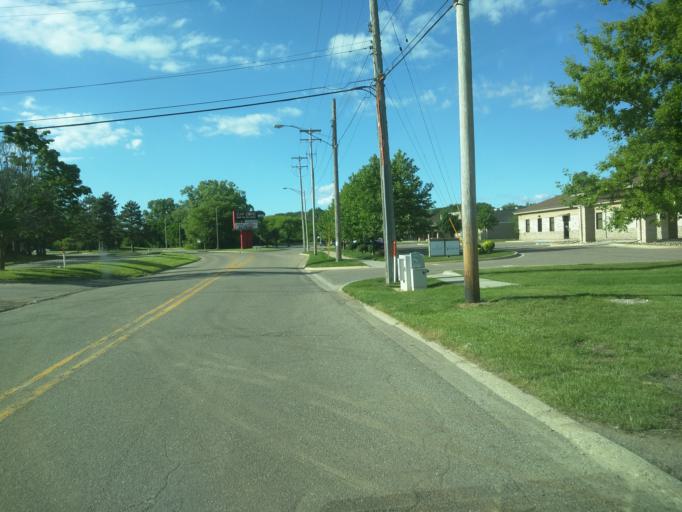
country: US
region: Michigan
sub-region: Eaton County
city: Waverly
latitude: 42.7425
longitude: -84.6194
